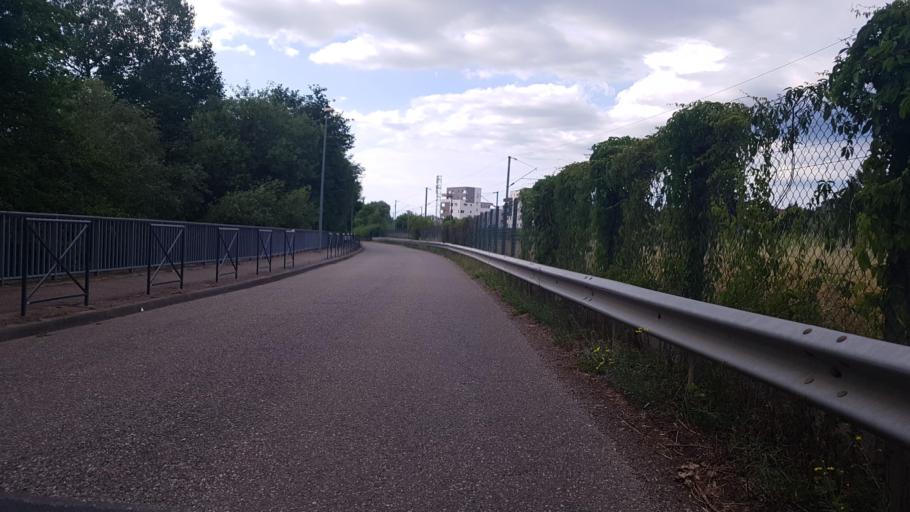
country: FR
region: Alsace
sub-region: Departement du Bas-Rhin
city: Brumath
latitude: 48.7344
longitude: 7.6990
